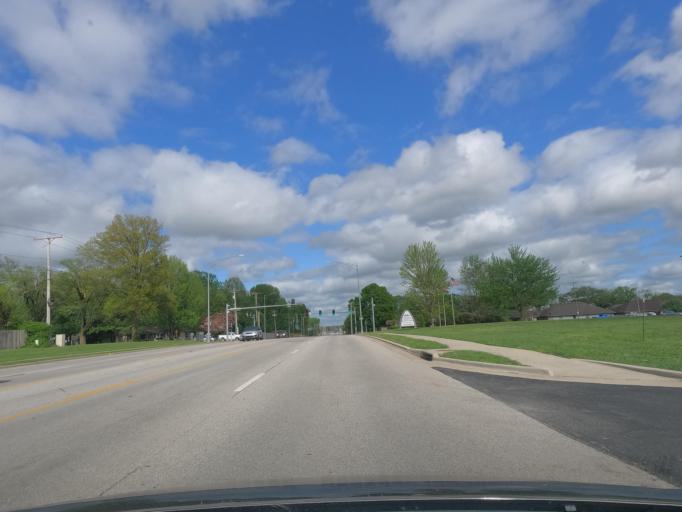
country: US
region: Missouri
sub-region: Greene County
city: Battlefield
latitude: 37.1382
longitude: -93.3058
